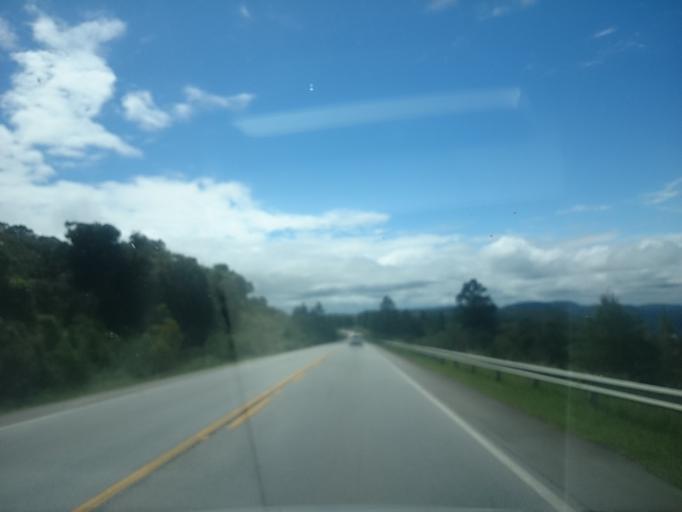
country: BR
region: Santa Catarina
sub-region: Anitapolis
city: Anitapolis
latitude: -27.6860
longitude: -49.1440
